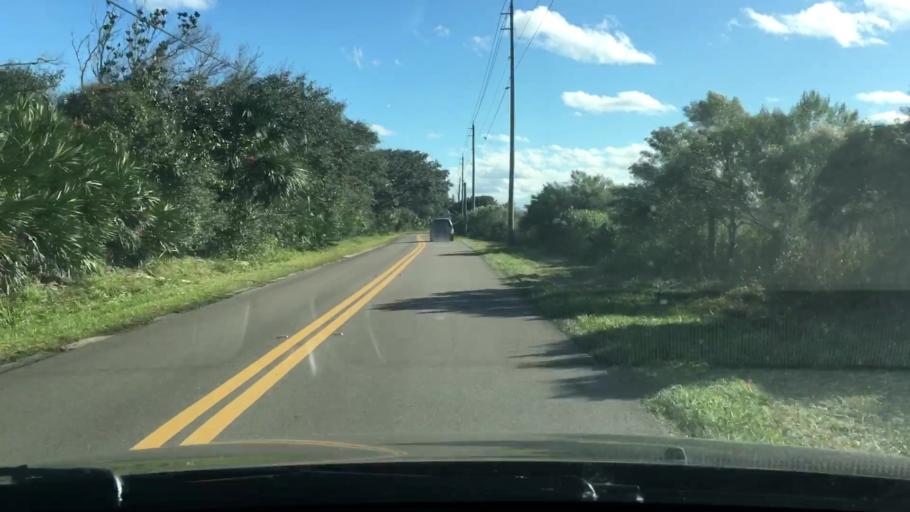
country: US
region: Florida
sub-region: Volusia County
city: Ormond-by-the-Sea
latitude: 29.4056
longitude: -81.0965
